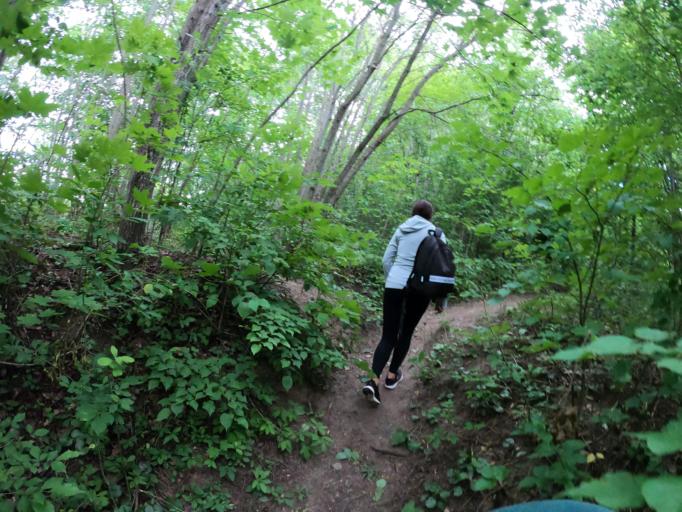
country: LT
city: Jieznas
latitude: 54.5121
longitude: 24.0883
